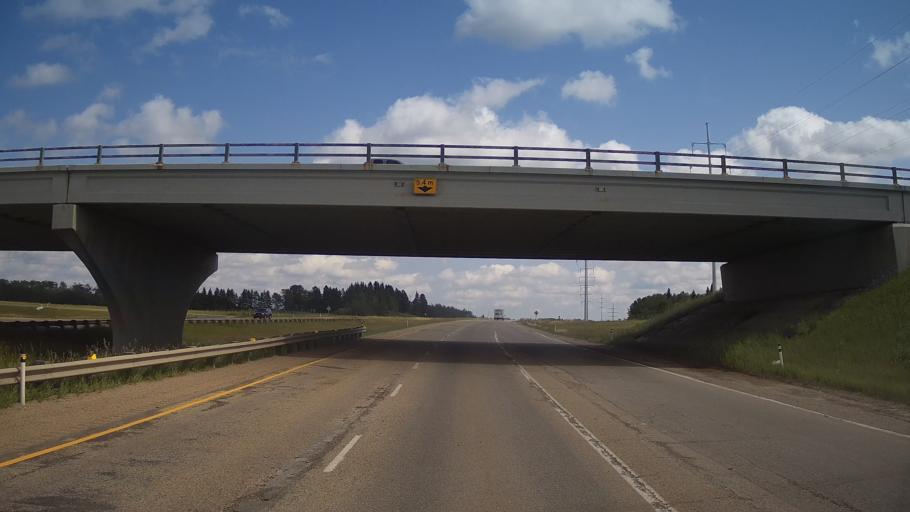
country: CA
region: Alberta
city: Sherwood Park
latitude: 53.4466
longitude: -113.2468
